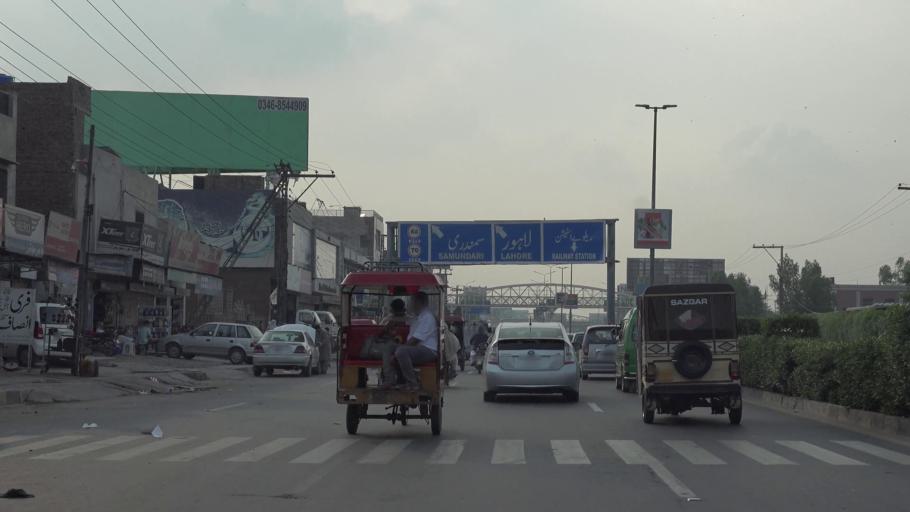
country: PK
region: Punjab
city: Faisalabad
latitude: 31.4185
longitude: 73.1062
